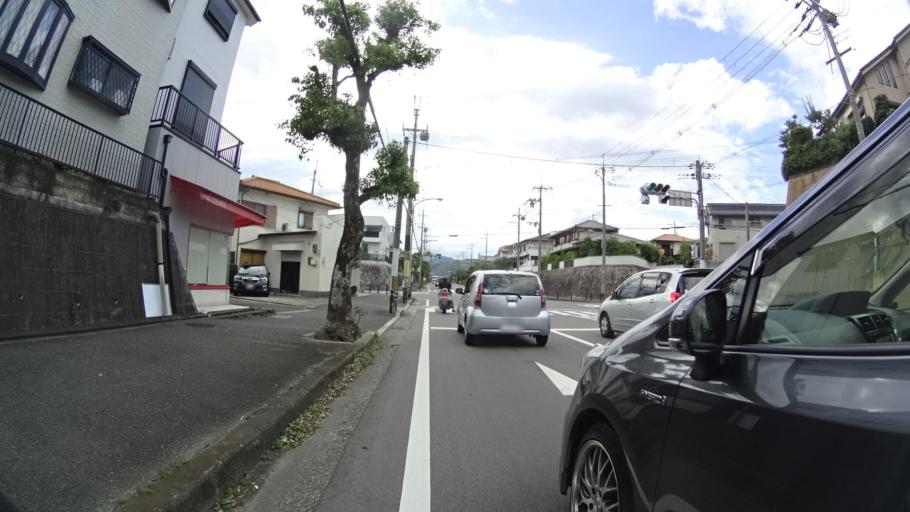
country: JP
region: Kyoto
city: Yawata
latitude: 34.8709
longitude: 135.6902
